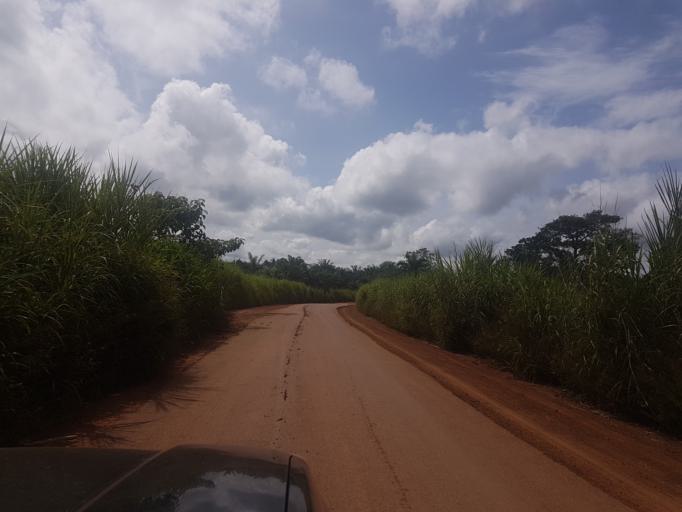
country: GN
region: Nzerekore
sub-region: Prefecture de Guekedou
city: Gueckedou
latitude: 8.6759
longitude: -10.1207
